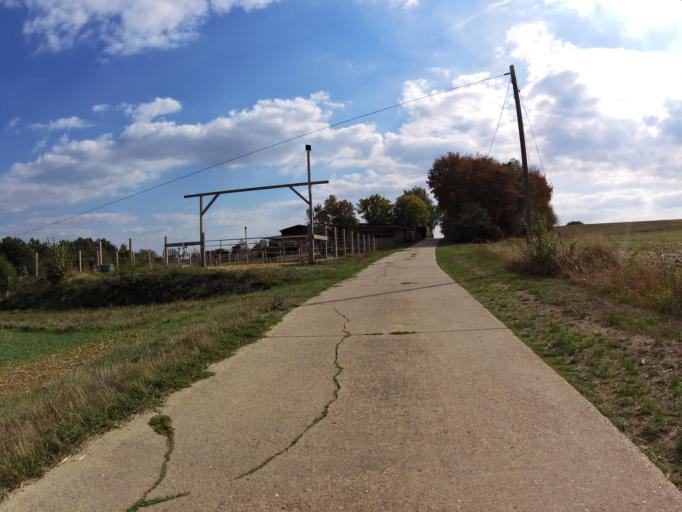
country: DE
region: Bavaria
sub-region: Regierungsbezirk Unterfranken
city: Hettstadt
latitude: 49.7913
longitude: 9.7956
